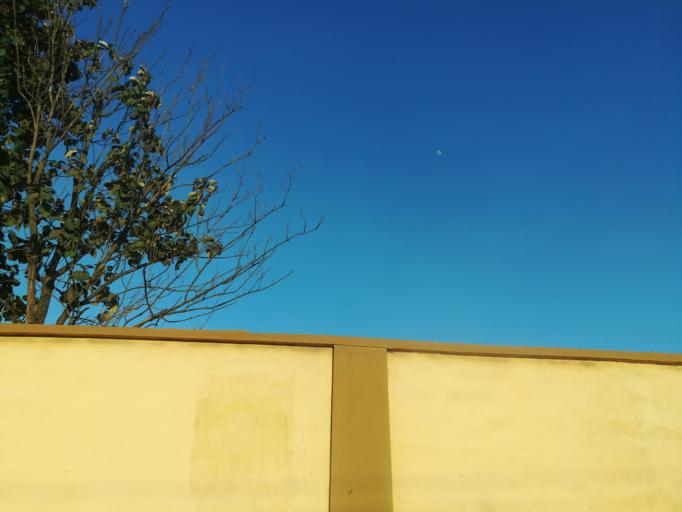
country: NG
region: Lagos
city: Ikorodu
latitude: 6.5967
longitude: 3.5179
